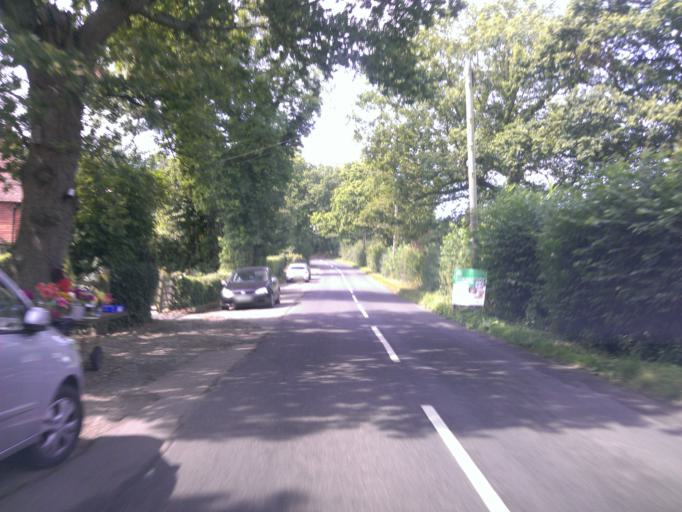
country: GB
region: England
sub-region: Kent
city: Edenbridge
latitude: 51.1993
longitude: 0.1149
